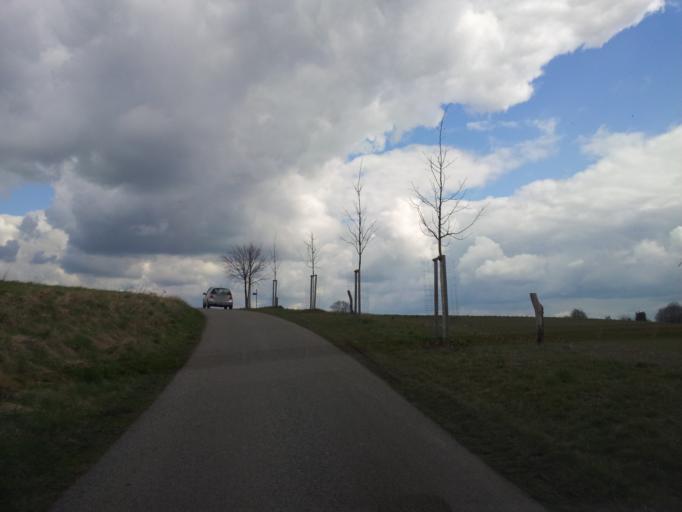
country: DE
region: Saxony
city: Panschwitz-Kuckau
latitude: 51.2156
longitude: 14.2013
